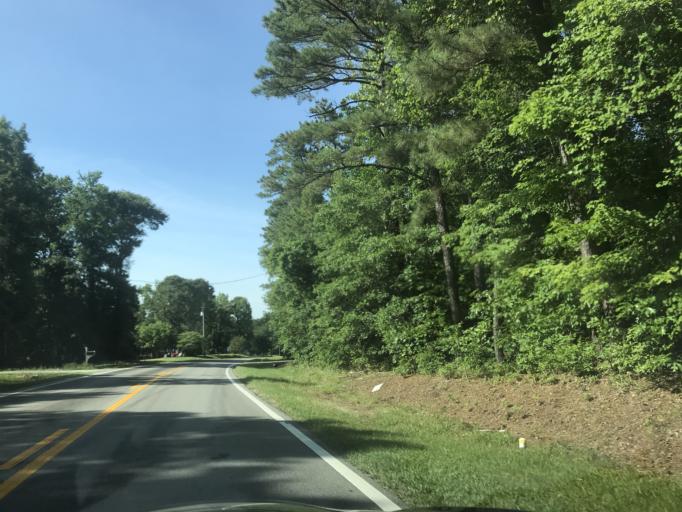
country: US
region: North Carolina
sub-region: Johnston County
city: Clayton
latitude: 35.5946
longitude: -78.5369
